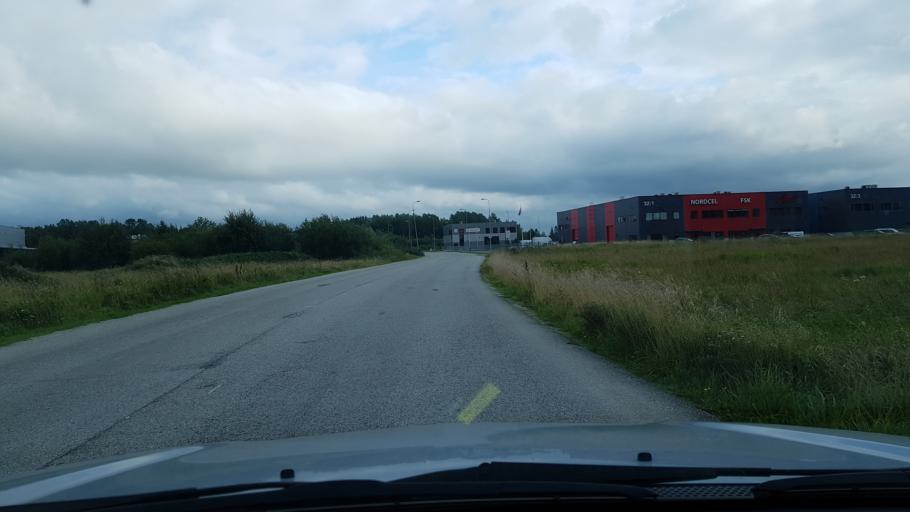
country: EE
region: Harju
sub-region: Rae vald
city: Jueri
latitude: 59.3965
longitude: 24.8248
